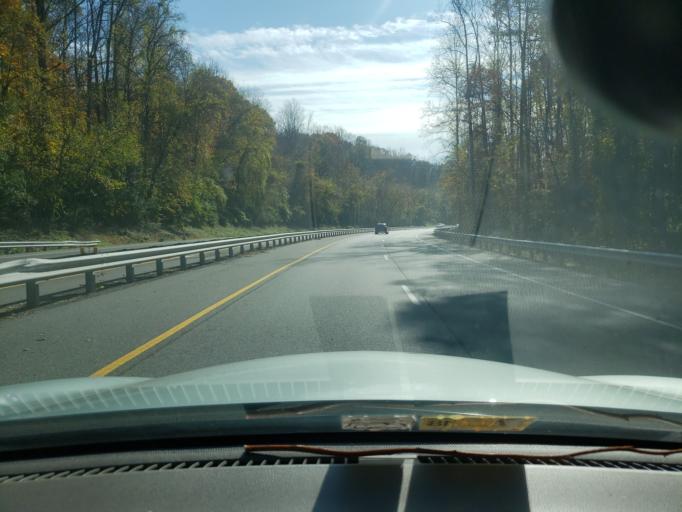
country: US
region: Maryland
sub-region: Montgomery County
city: Cabin John
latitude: 38.9773
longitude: -77.1508
